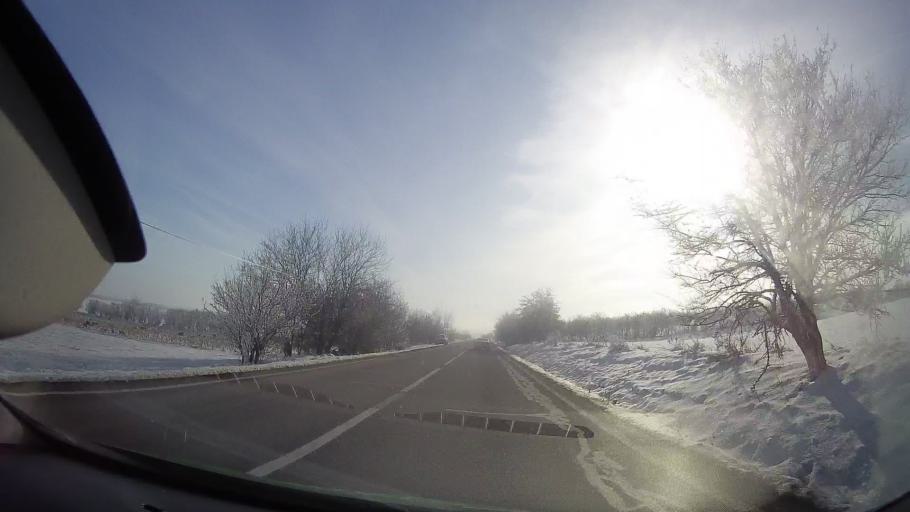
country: RO
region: Neamt
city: Bodesti
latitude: 47.0109
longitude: 26.4242
